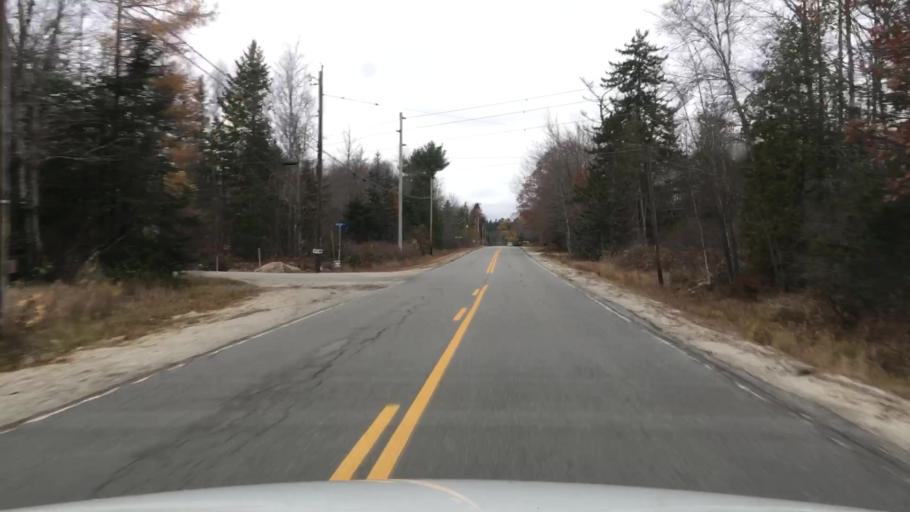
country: US
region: Maine
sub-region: Hancock County
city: Penobscot
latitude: 44.4196
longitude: -68.6164
